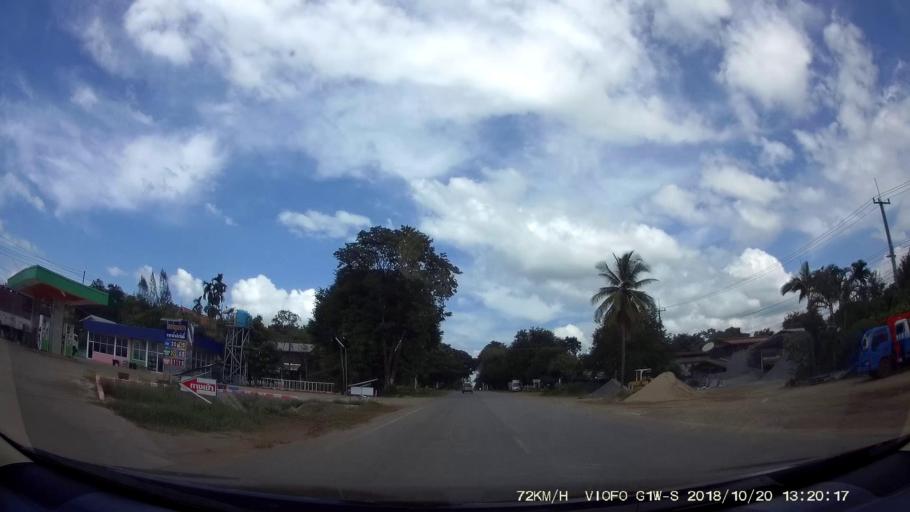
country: TH
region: Chaiyaphum
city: Khon San
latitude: 16.5466
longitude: 101.9034
